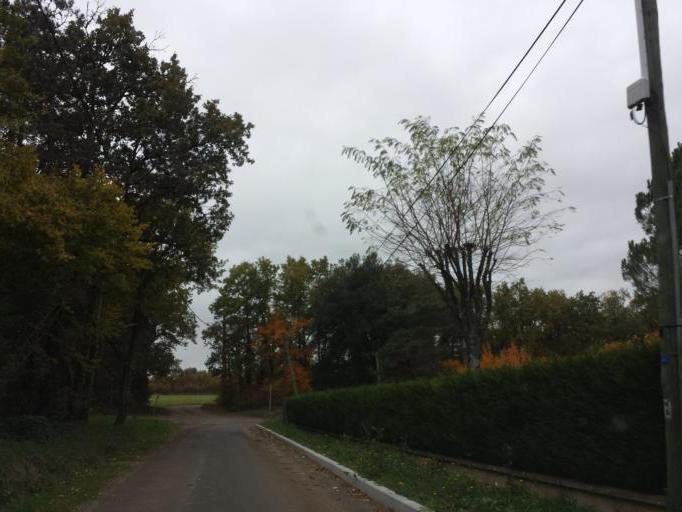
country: FR
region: Poitou-Charentes
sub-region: Departement de la Charente
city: Puymoyen
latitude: 45.6000
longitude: 0.1772
